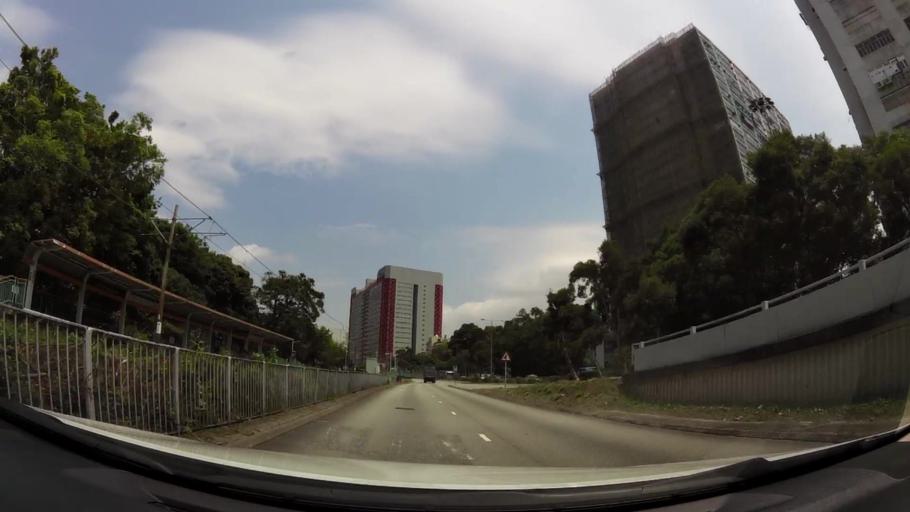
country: HK
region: Tuen Mun
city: Tuen Mun
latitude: 22.3902
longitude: 113.9670
